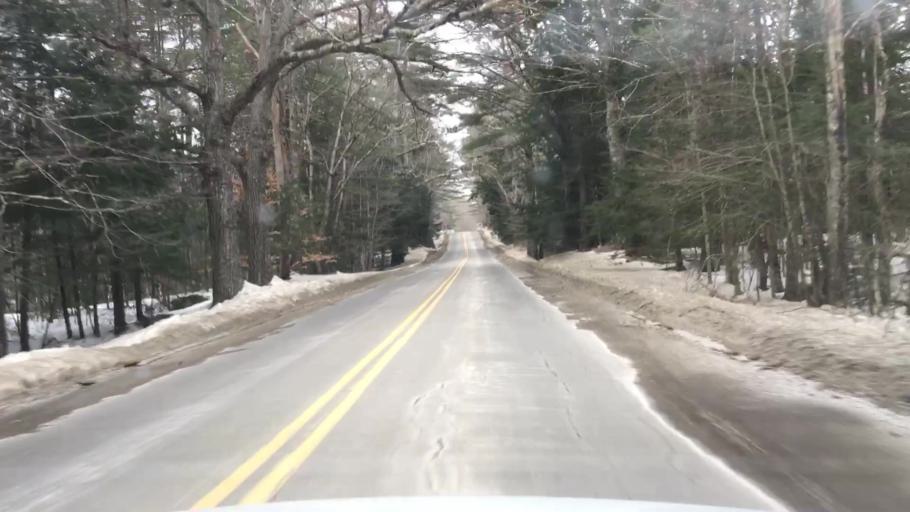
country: US
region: Maine
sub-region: Lincoln County
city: Whitefield
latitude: 44.2435
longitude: -69.6304
